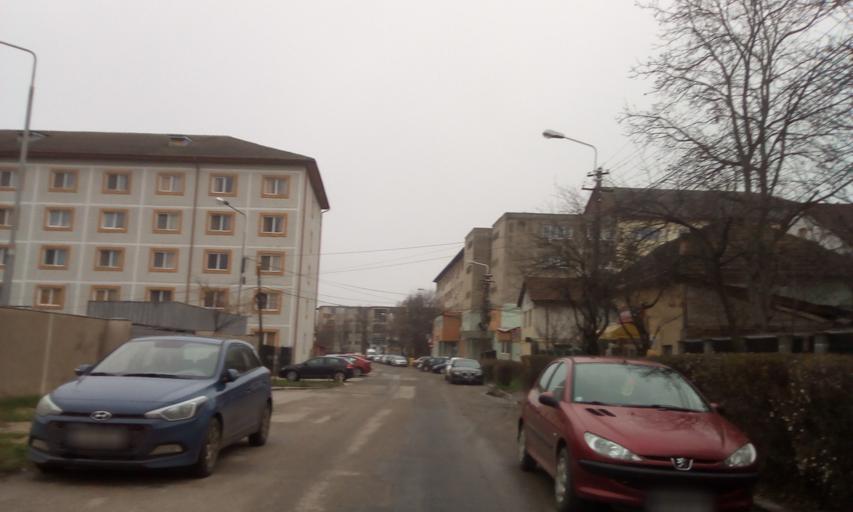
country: RO
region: Timis
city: Timisoara
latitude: 45.7514
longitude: 21.2437
